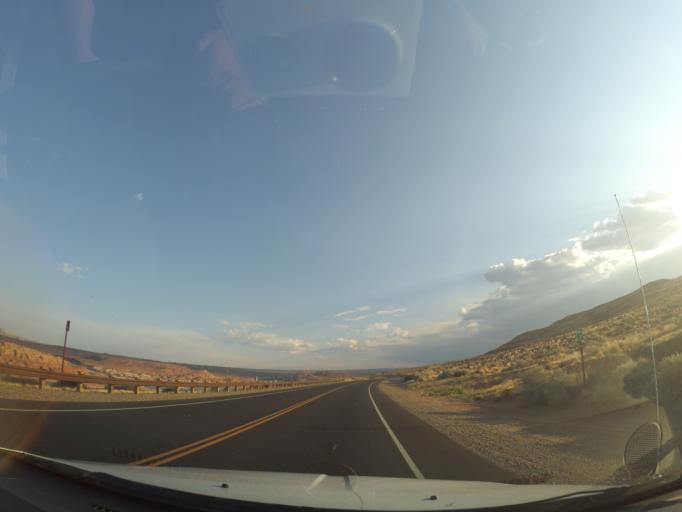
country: US
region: Arizona
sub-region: Coconino County
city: Page
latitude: 36.9673
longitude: -111.4899
